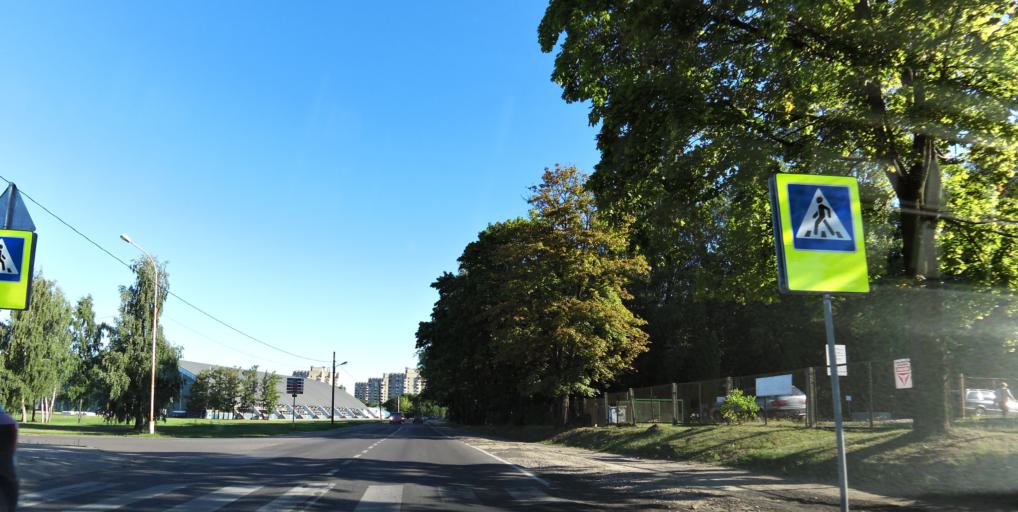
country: LT
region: Vilnius County
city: Seskine
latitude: 54.7056
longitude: 25.2378
